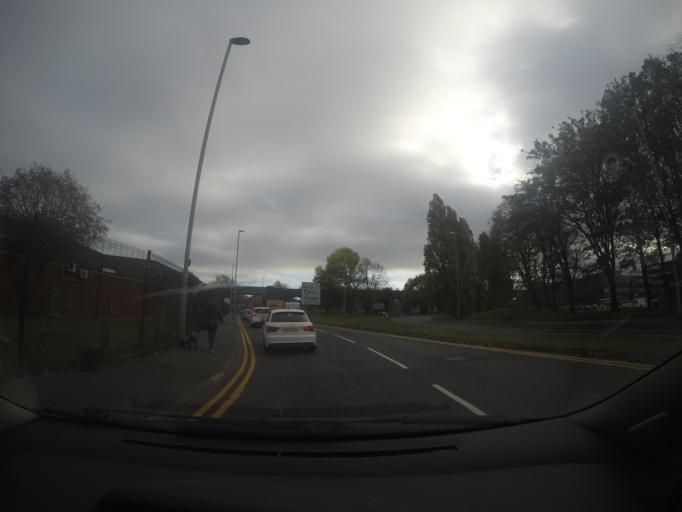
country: GB
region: England
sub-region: City and Borough of Leeds
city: Leeds
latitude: 53.7886
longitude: -1.5639
